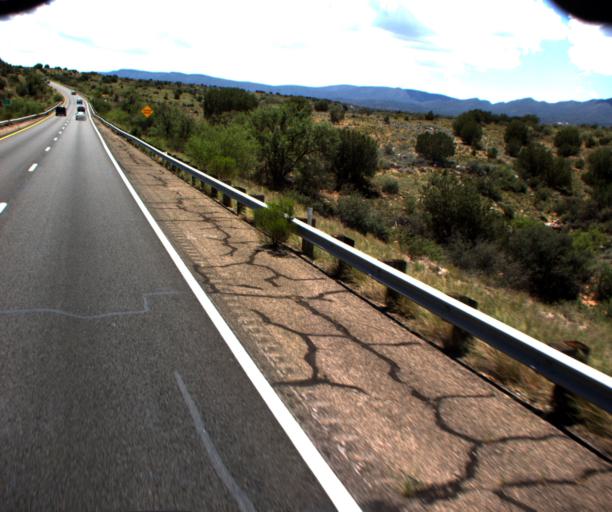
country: US
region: Arizona
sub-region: Yavapai County
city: Verde Village
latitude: 34.6701
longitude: -111.9704
